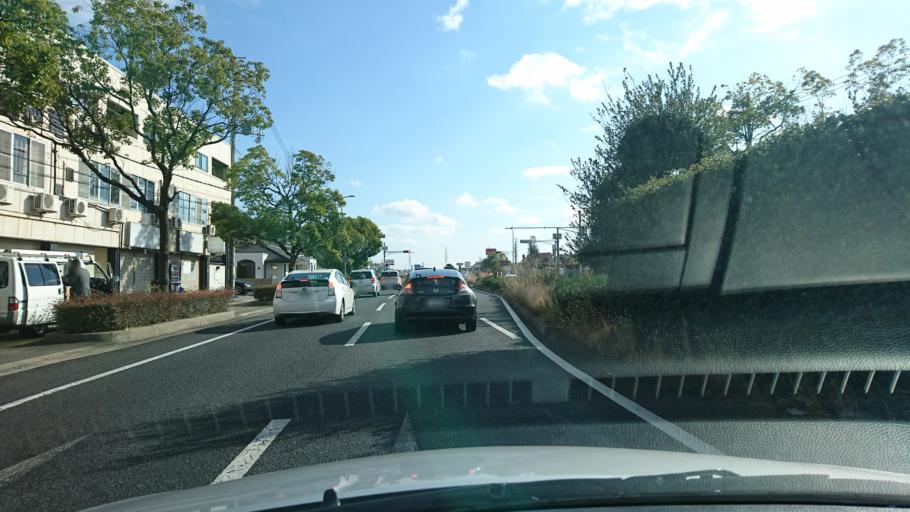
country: JP
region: Hyogo
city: Kakogawacho-honmachi
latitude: 34.7807
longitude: 134.7883
